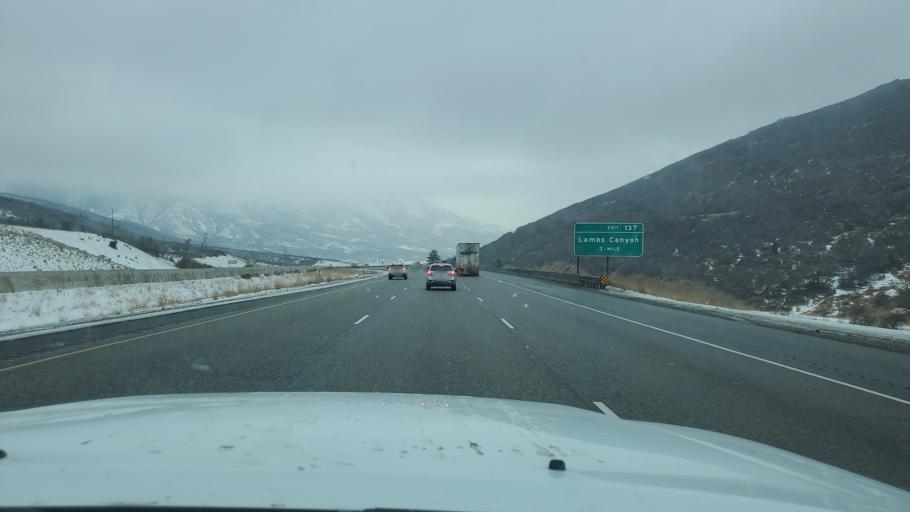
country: US
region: Utah
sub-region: Summit County
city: Summit Park
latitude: 40.7463
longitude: -111.6433
